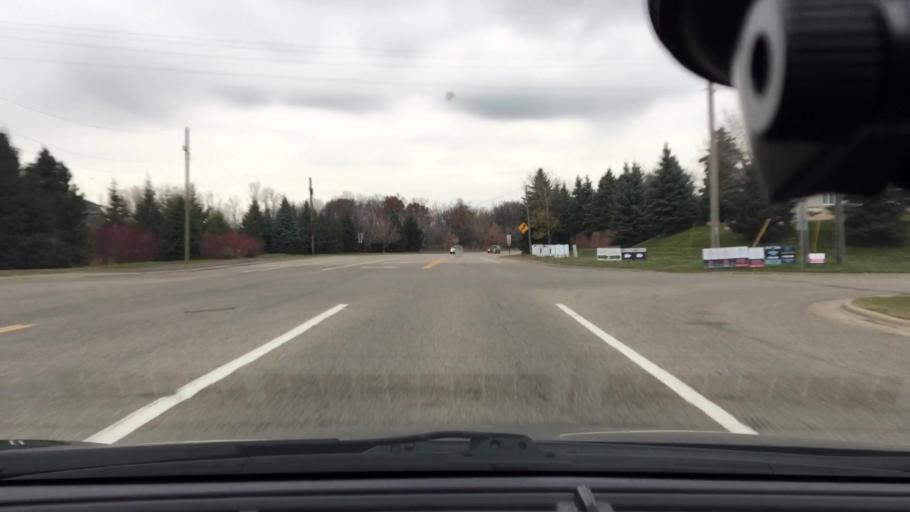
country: US
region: Minnesota
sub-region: Hennepin County
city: Corcoran
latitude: 45.0491
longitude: -93.5248
